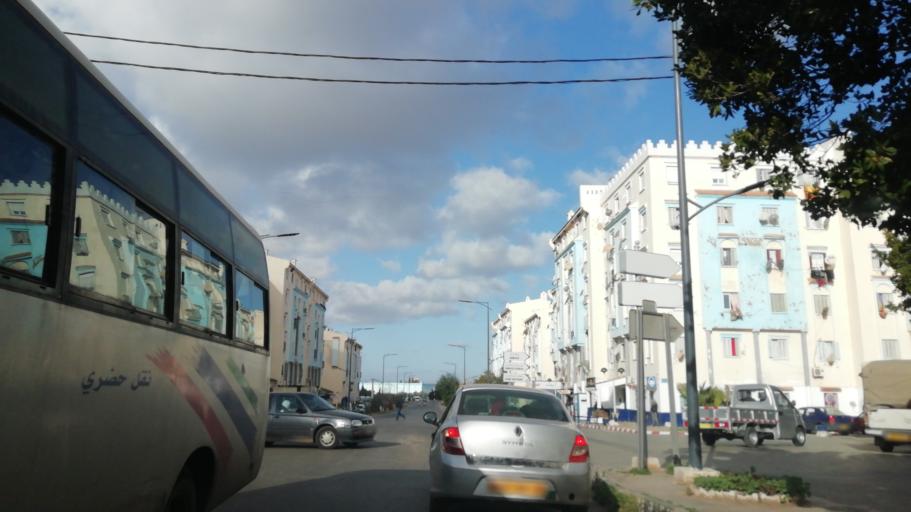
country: DZ
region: Ain Temouchent
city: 'Ain Temouchent
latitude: 35.3019
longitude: -1.1540
